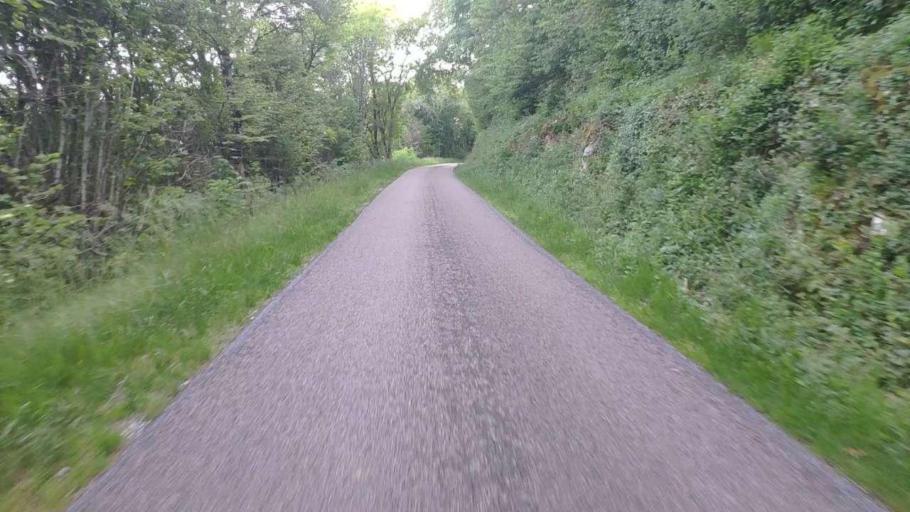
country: FR
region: Franche-Comte
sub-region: Departement du Jura
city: Perrigny
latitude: 46.7189
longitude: 5.6050
